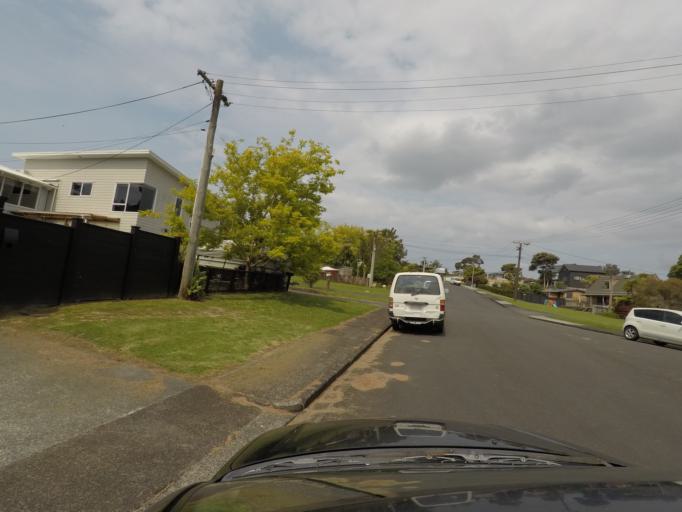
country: NZ
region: Auckland
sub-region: Auckland
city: Rosebank
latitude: -36.8315
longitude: 174.6432
